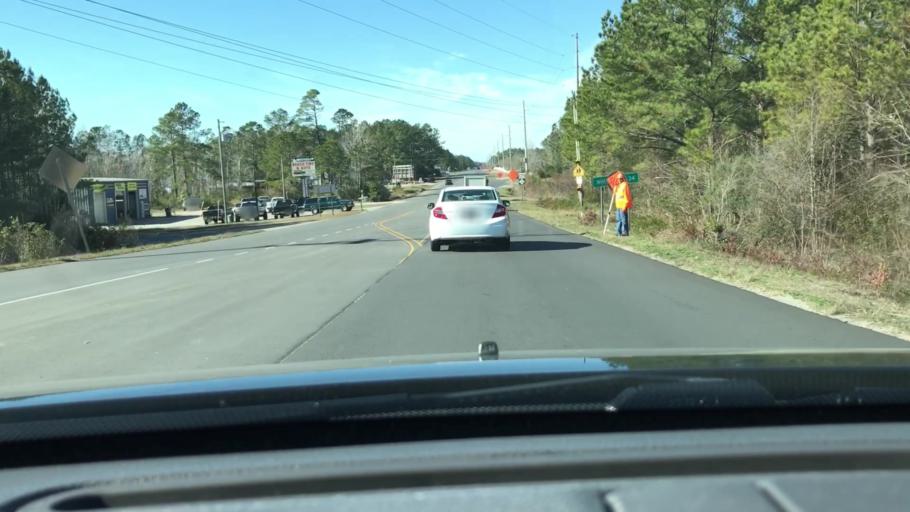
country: US
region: North Carolina
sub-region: Brunswick County
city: Shallotte
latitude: 33.9774
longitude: -78.4070
